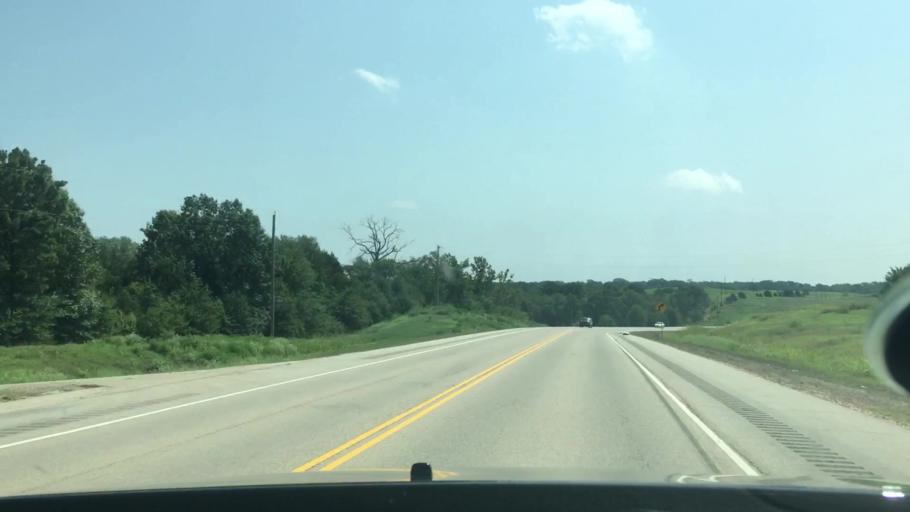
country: US
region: Oklahoma
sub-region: Atoka County
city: Atoka
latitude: 34.2892
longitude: -95.9610
